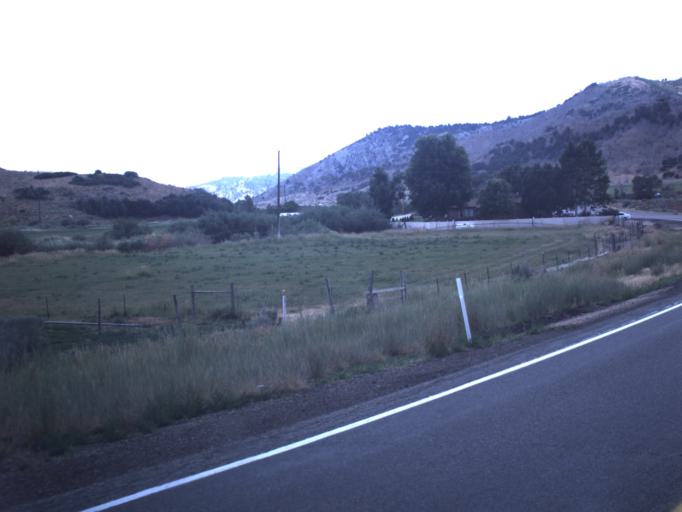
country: US
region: Utah
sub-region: Juab County
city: Nephi
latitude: 39.7170
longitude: -111.7264
